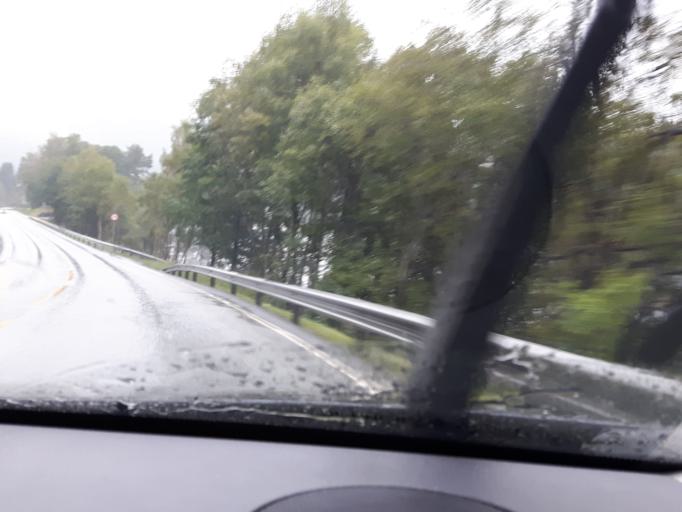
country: NO
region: Vest-Agder
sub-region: Lindesnes
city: Vigeland
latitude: 58.0676
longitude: 7.3514
